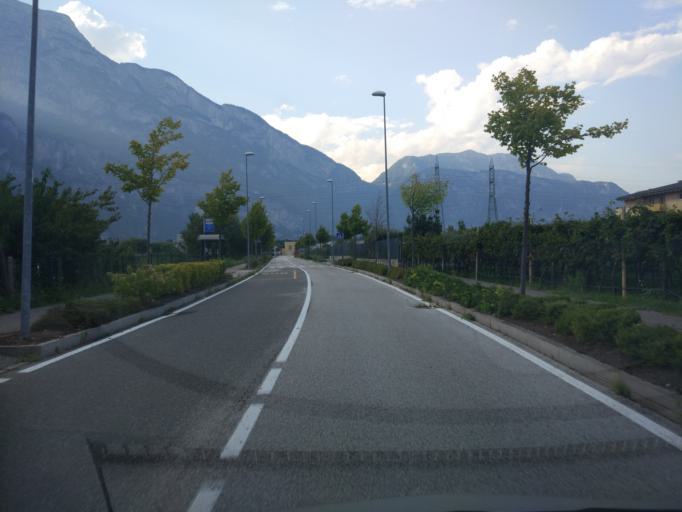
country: IT
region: Trentino-Alto Adige
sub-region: Provincia di Trento
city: Meano
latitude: 46.1253
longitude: 11.0986
